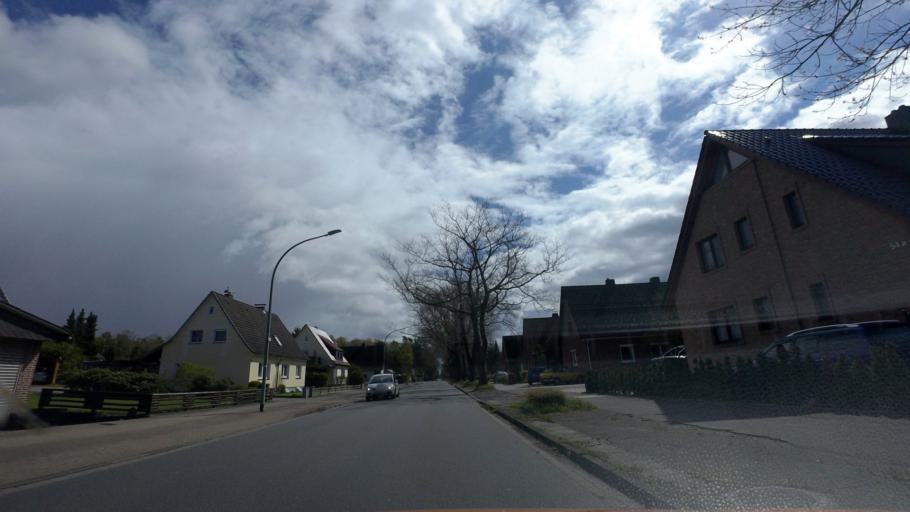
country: DE
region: Lower Saxony
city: Schneverdingen
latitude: 53.1089
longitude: 9.8102
